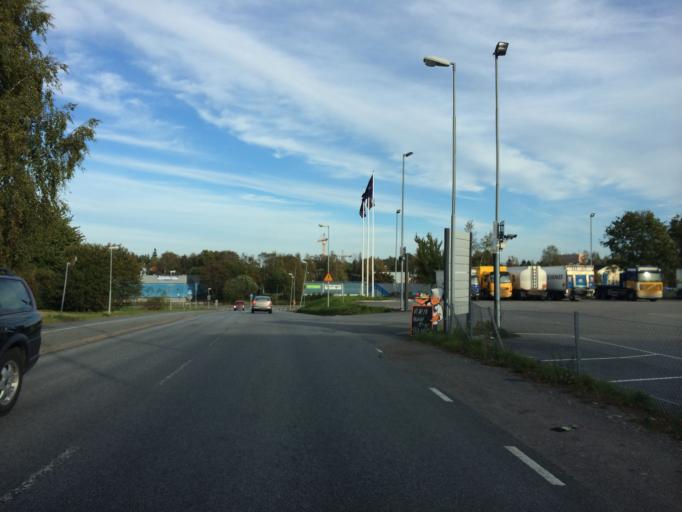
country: SE
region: Stockholm
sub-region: Sollentuna Kommun
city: Sollentuna
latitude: 59.4336
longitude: 17.9283
